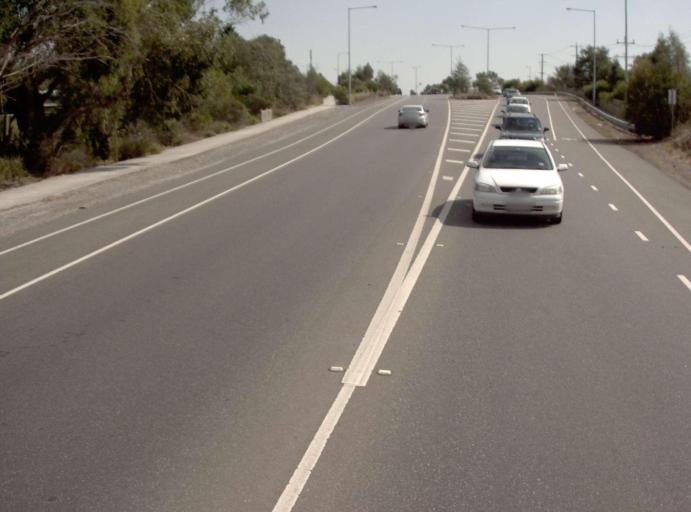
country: AU
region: Victoria
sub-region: Knox
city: Knoxfield
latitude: -37.9113
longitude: 145.2742
